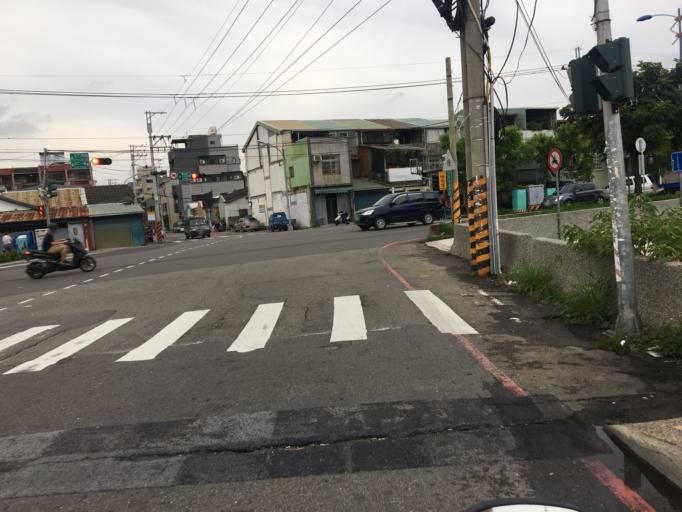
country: TW
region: Taiwan
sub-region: Taichung City
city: Taichung
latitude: 24.1024
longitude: 120.7010
